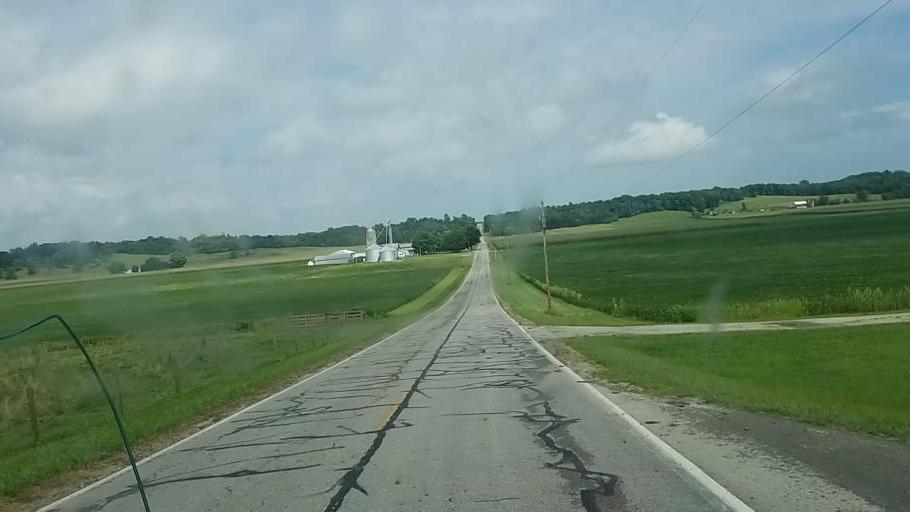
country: US
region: Ohio
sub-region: Logan County
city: West Liberty
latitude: 40.2316
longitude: -83.6937
